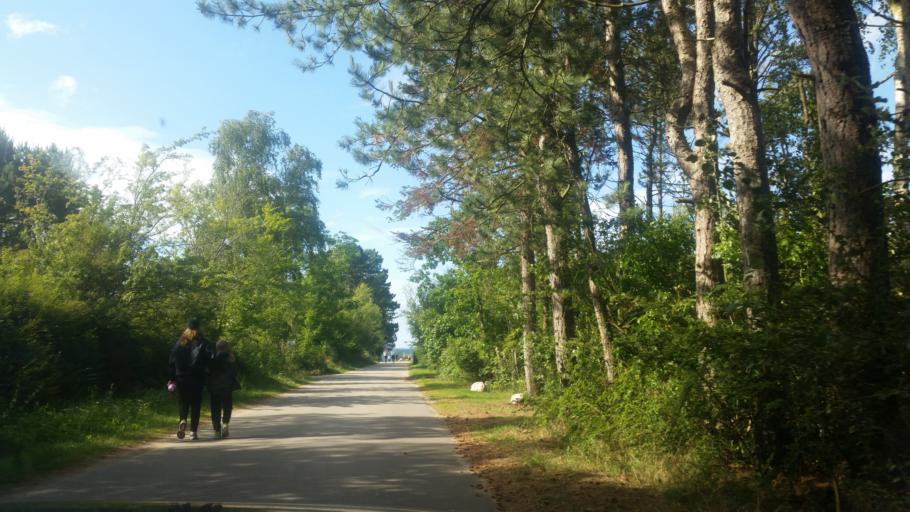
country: DK
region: Zealand
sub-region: Odsherred Kommune
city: Horve
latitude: 55.8286
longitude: 11.3961
